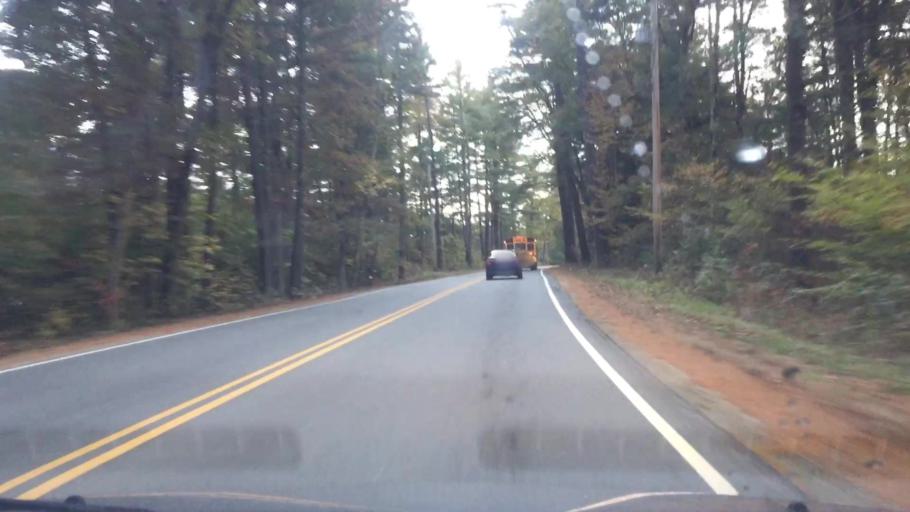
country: US
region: New Hampshire
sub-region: Cheshire County
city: Swanzey
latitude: 42.8424
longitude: -72.2797
